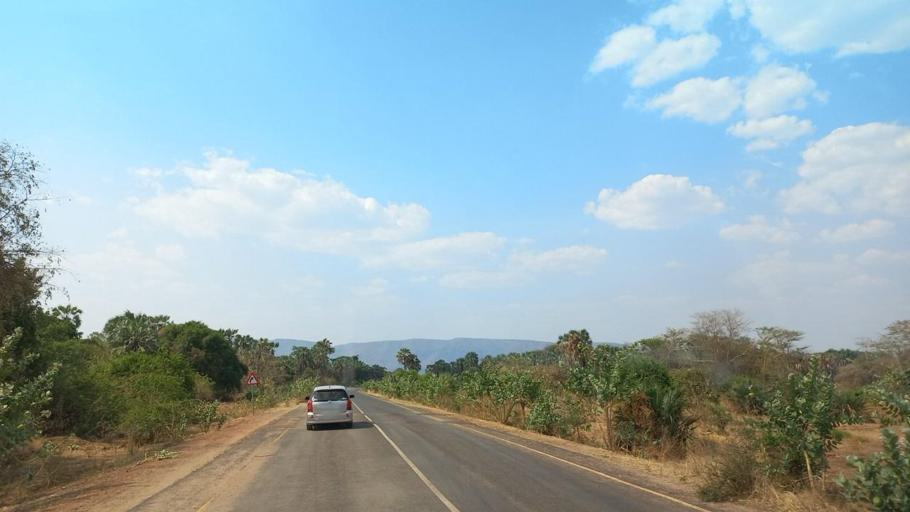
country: ZM
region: Lusaka
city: Luangwa
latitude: -15.0929
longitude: 30.1927
